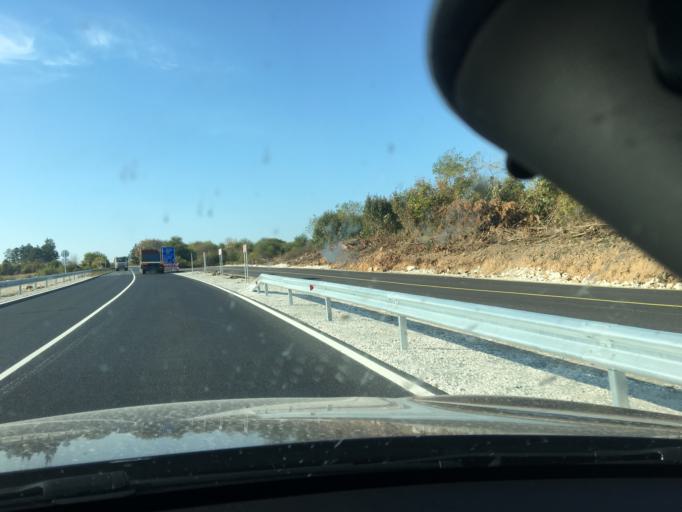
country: BG
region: Lovech
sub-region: Obshtina Yablanitsa
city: Yablanitsa
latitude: 43.0581
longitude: 24.2206
